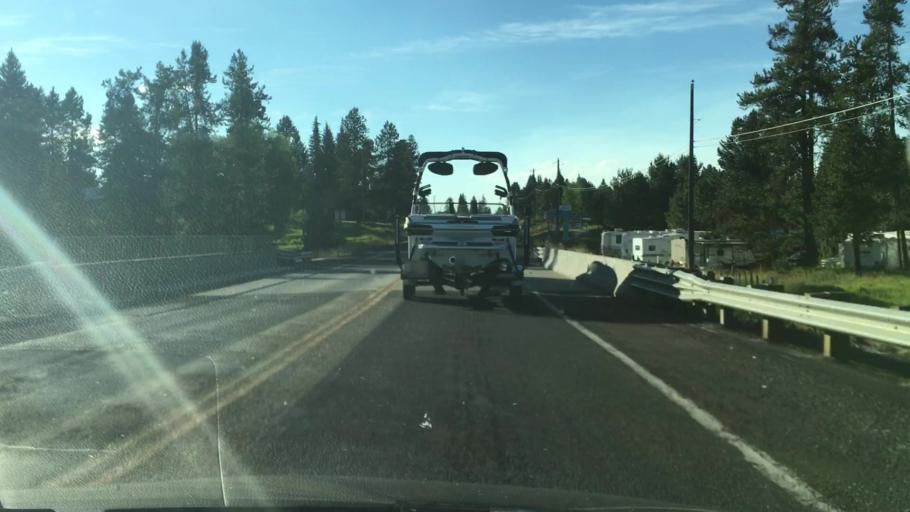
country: US
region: Idaho
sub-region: Valley County
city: McCall
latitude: 44.7269
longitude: -116.0742
